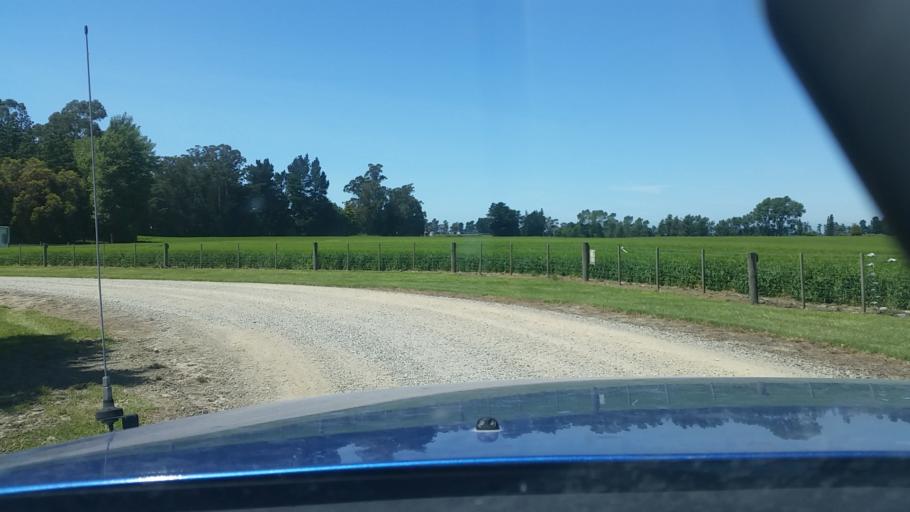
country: NZ
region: Canterbury
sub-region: Ashburton District
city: Ashburton
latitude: -43.9562
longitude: 171.8272
